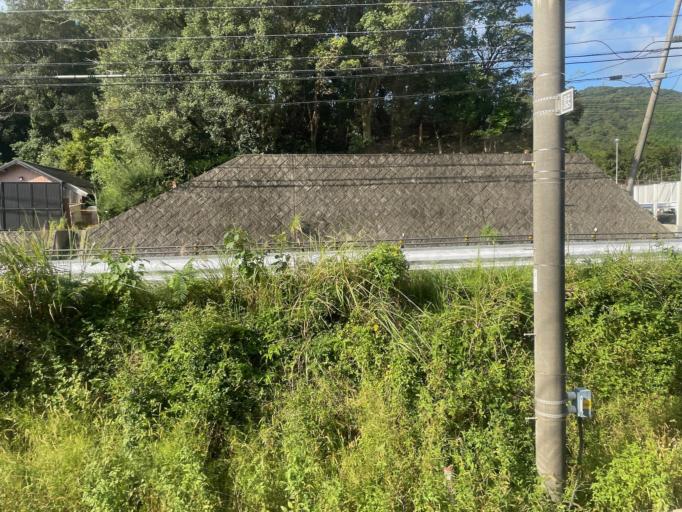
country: JP
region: Mie
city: Toba
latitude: 34.3990
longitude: 136.8136
